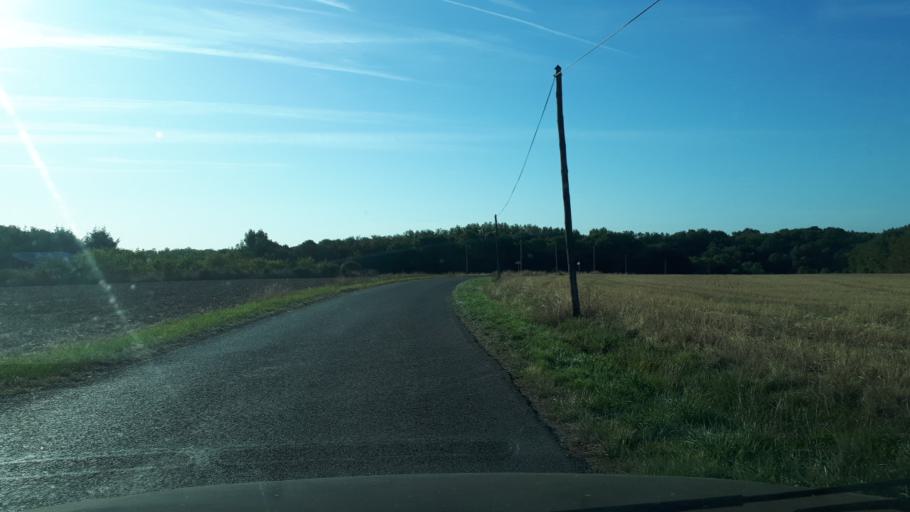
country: FR
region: Centre
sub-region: Departement d'Indre-et-Loire
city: Chateau-Renault
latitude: 47.6597
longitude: 0.9399
